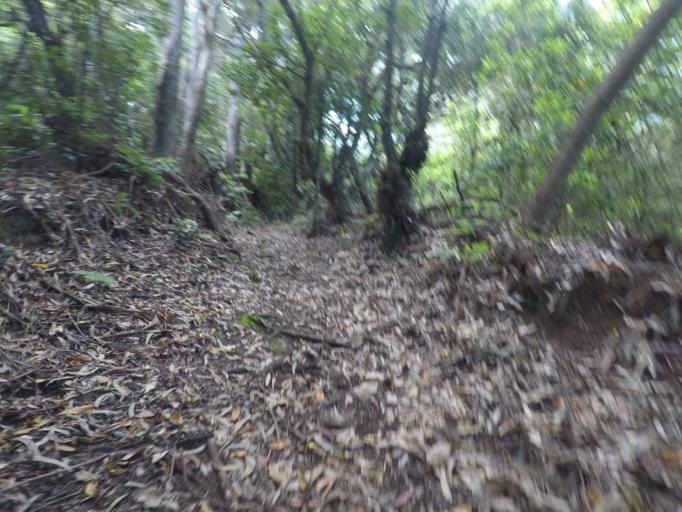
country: PT
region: Madeira
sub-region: Porto Moniz
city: Porto Moniz
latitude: 32.8347
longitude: -17.1408
